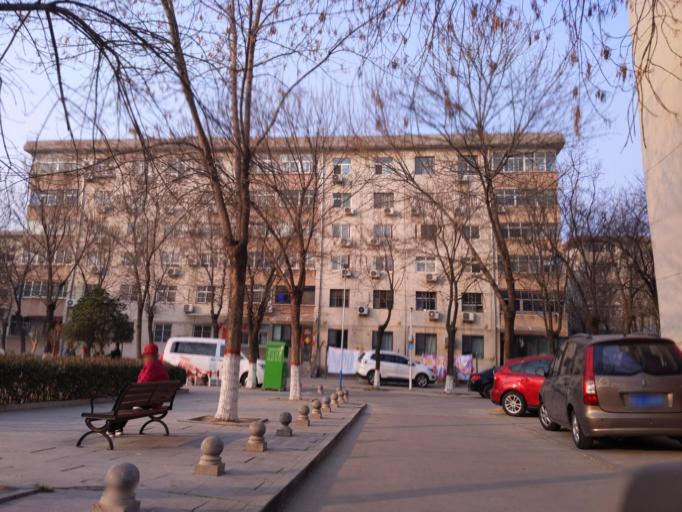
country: CN
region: Henan Sheng
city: Zhongyuanlu
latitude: 35.7816
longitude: 115.0587
